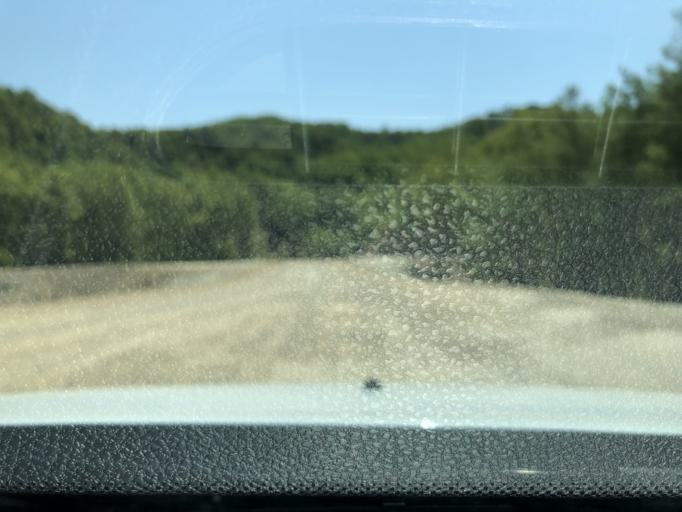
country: TR
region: Antalya
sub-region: Manavgat
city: Manavgat
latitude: 36.8331
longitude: 31.5312
